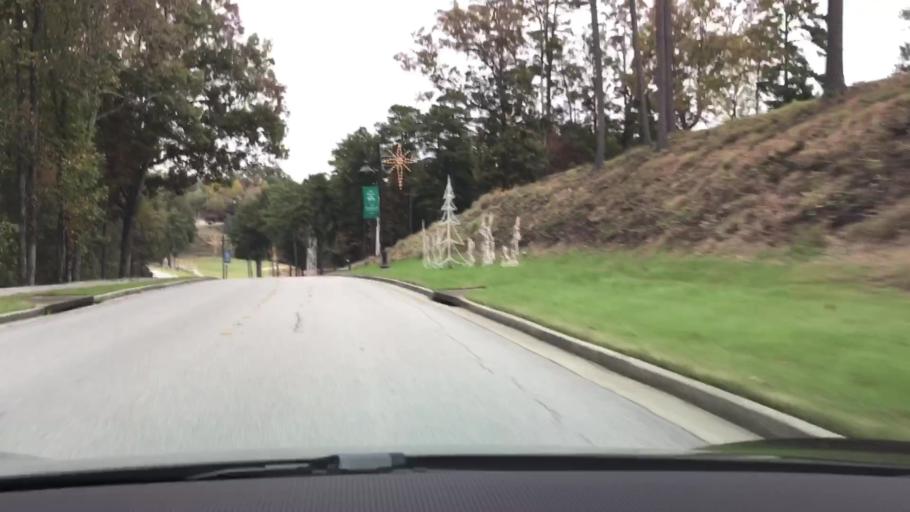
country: US
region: Georgia
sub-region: Gwinnett County
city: Buford
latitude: 34.1811
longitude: -84.0196
